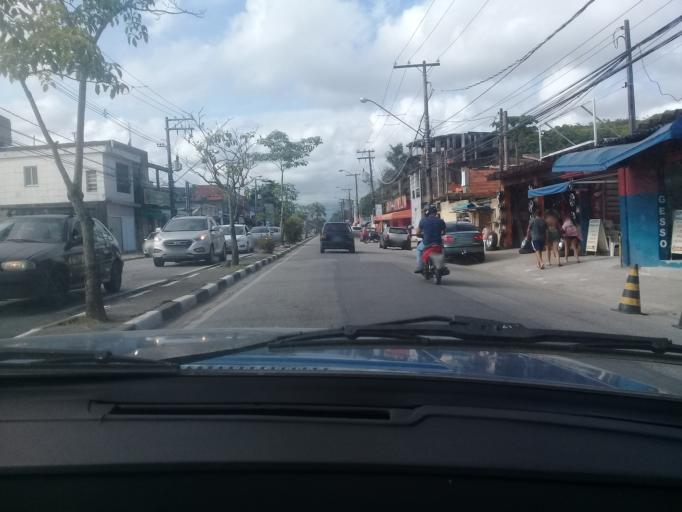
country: BR
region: Sao Paulo
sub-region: Guaruja
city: Guaruja
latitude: -24.0039
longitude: -46.2736
